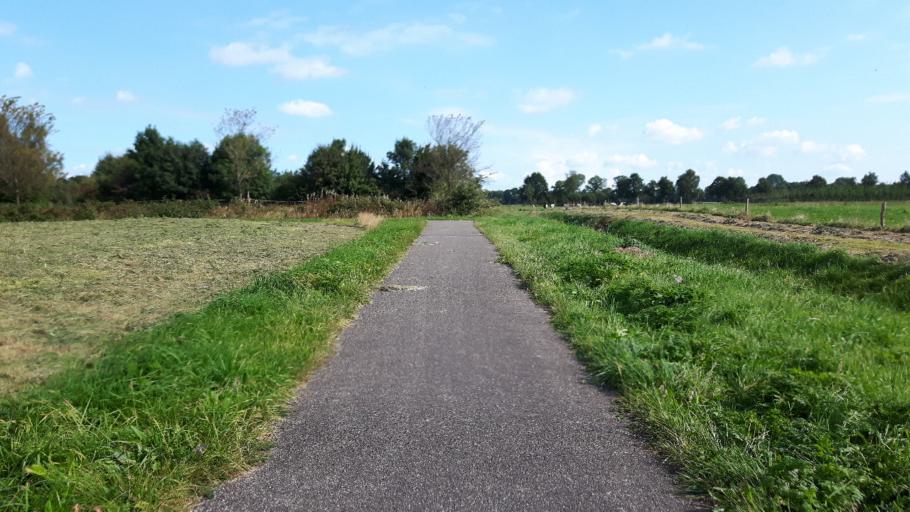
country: NL
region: Groningen
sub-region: Gemeente Leek
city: Leek
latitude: 53.1259
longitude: 6.4599
